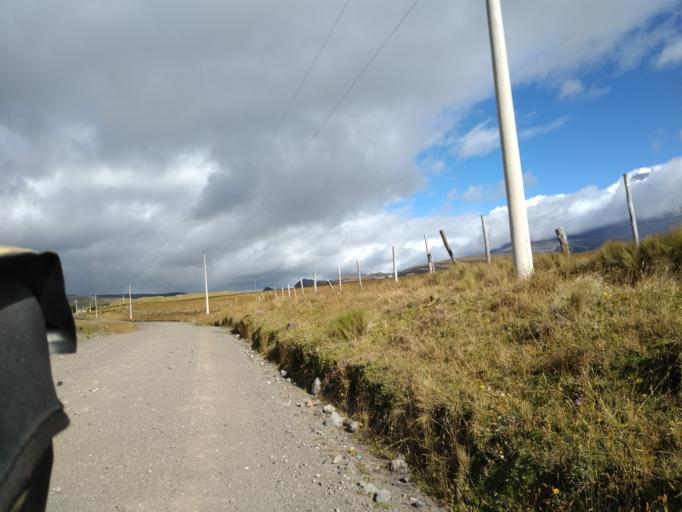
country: EC
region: Pichincha
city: Machachi
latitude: -0.5591
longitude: -78.4515
